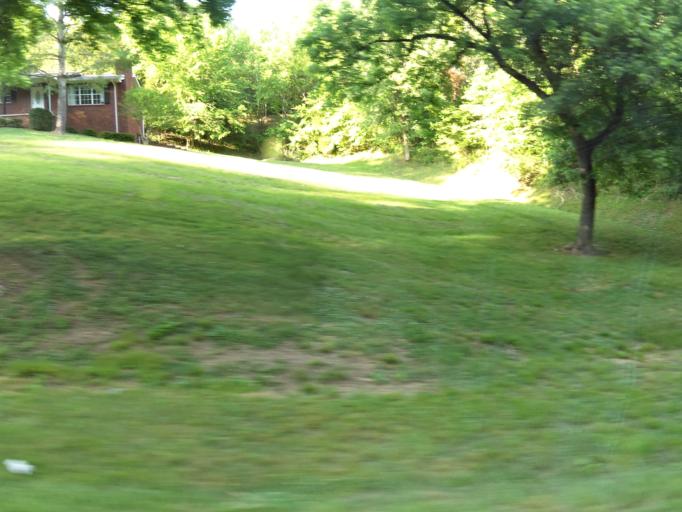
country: US
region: Tennessee
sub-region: Sevier County
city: Seymour
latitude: 35.8527
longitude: -83.7157
